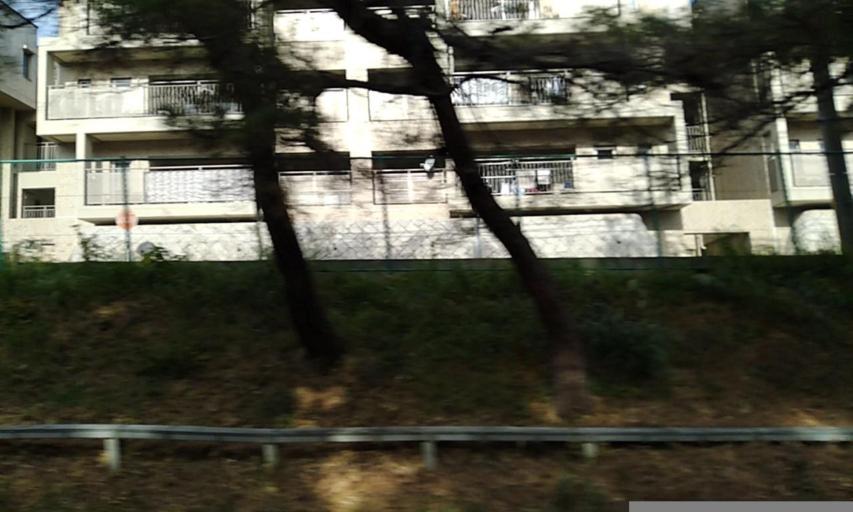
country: JP
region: Hyogo
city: Ashiya
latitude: 34.7417
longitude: 135.3185
